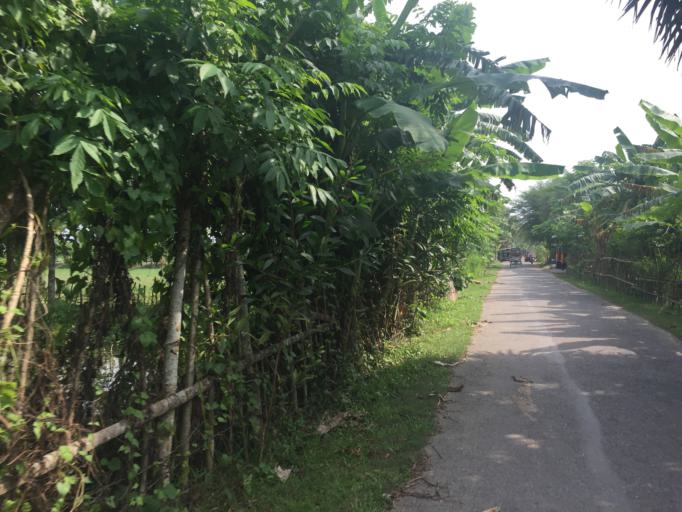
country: BD
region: Barisal
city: Mathba
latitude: 22.2515
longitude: 89.9161
